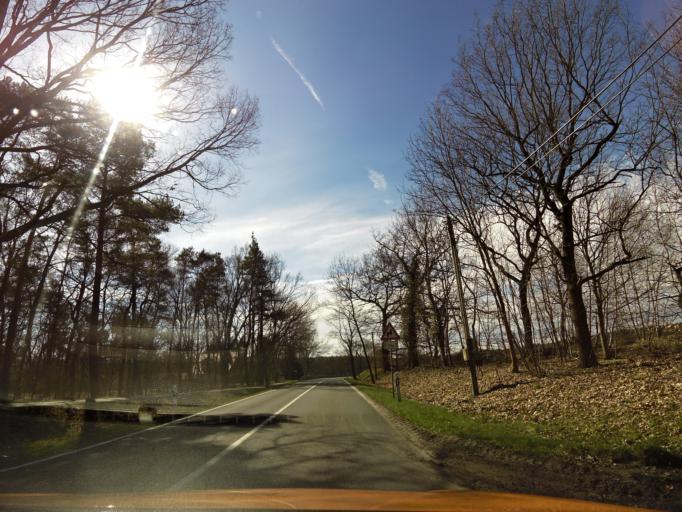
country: DE
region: Brandenburg
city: Belzig
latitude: 52.1747
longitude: 12.6219
